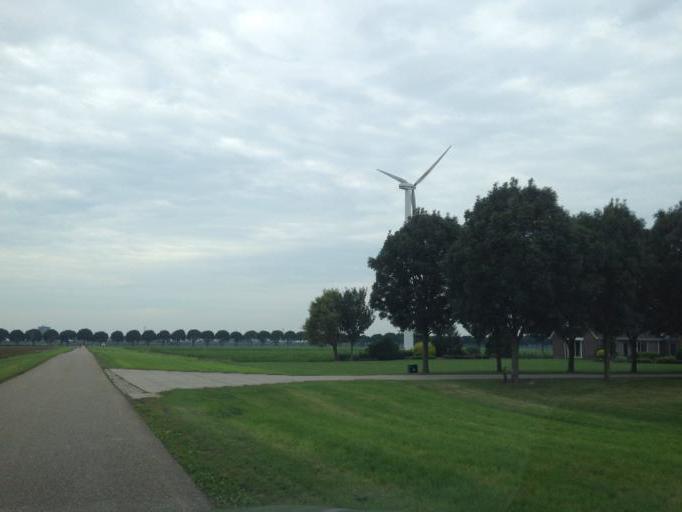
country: NL
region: Flevoland
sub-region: Gemeente Almere
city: Almere Stad
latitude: 52.3816
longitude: 5.3320
